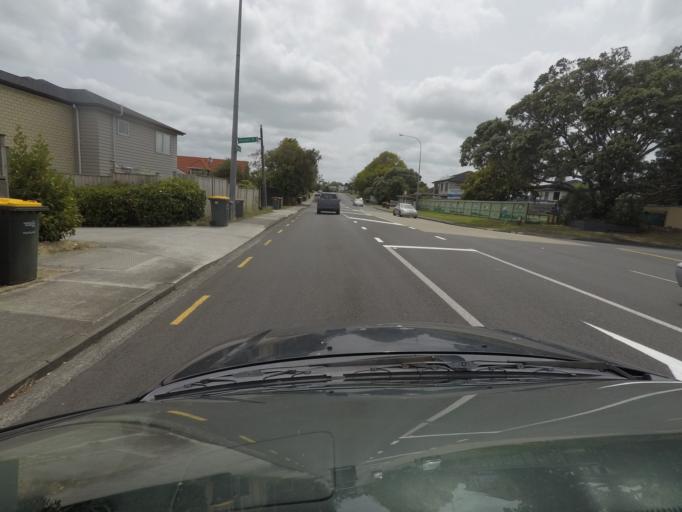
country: NZ
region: Auckland
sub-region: Auckland
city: Pakuranga
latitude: -36.8983
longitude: 174.9200
